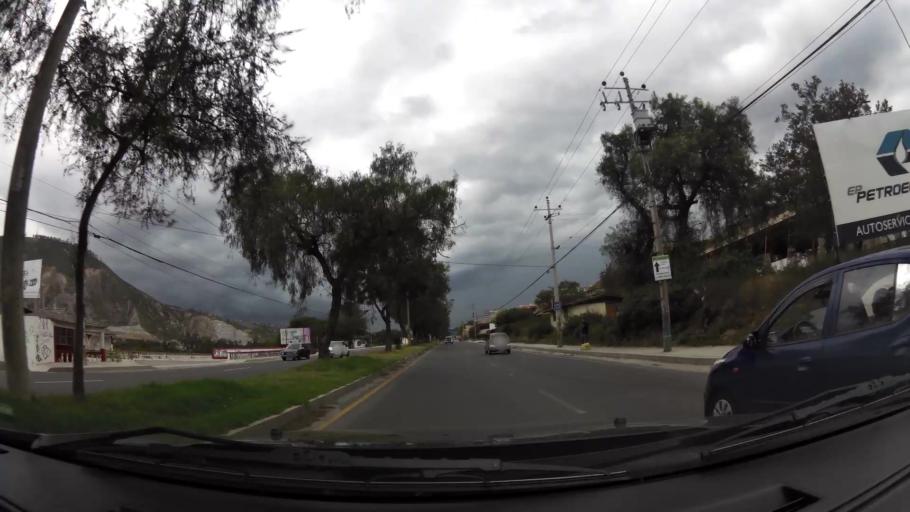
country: EC
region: Pichincha
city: Quito
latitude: -0.0431
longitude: -78.4555
